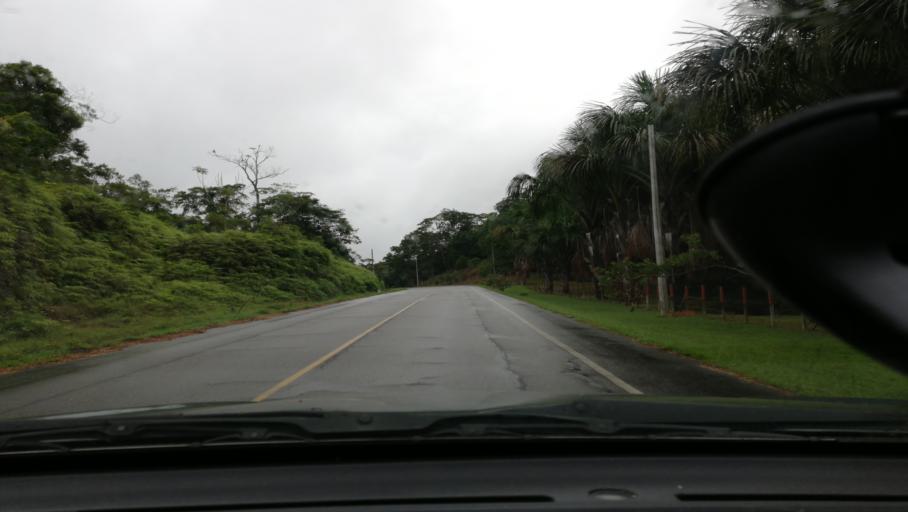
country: PE
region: Loreto
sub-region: Provincia de Loreto
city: Nauta
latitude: -4.4173
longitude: -73.5843
